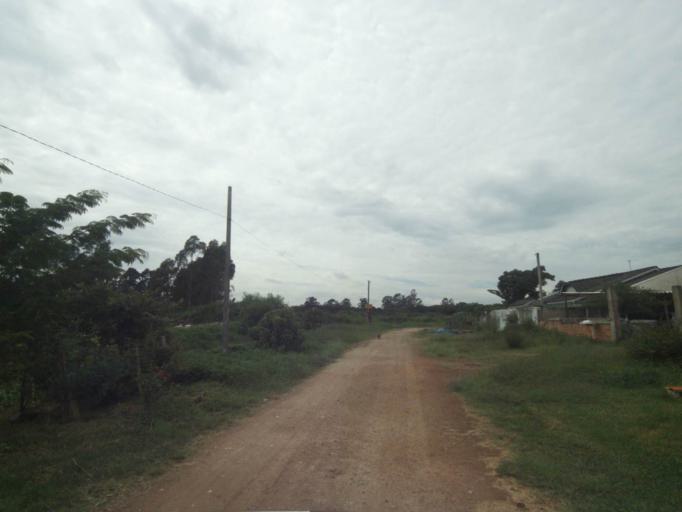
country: BR
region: Parana
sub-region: Pinhais
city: Pinhais
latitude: -25.4746
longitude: -49.1886
